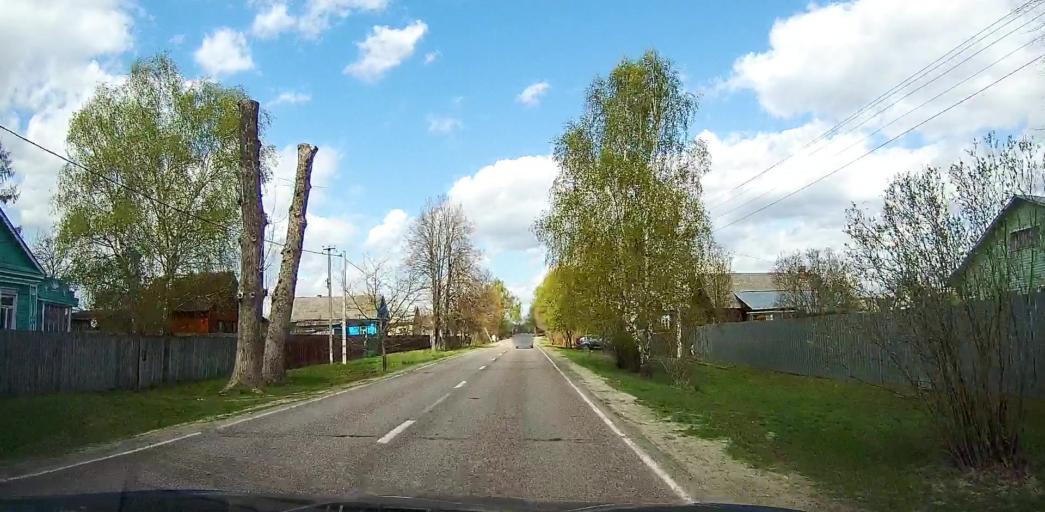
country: RU
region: Moskovskaya
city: Davydovo
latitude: 55.5785
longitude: 38.8230
